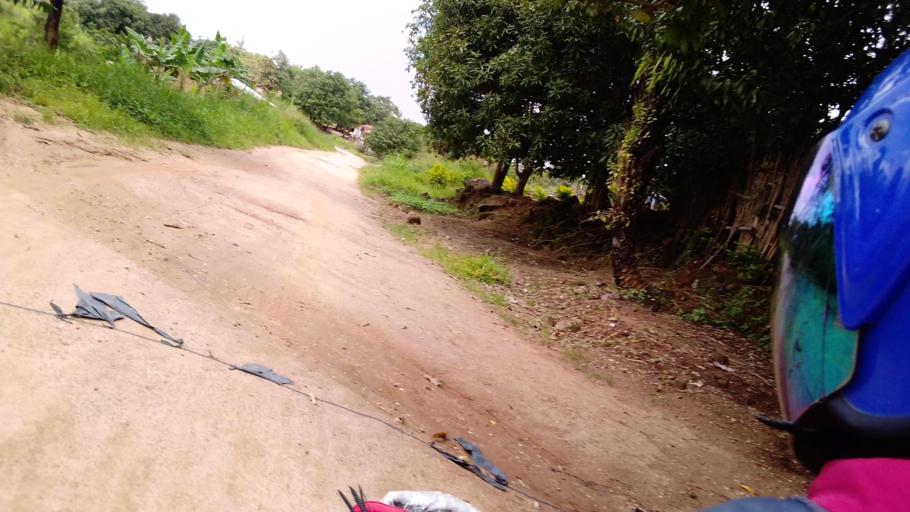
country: SL
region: Eastern Province
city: Koyima
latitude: 8.6942
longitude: -11.0106
